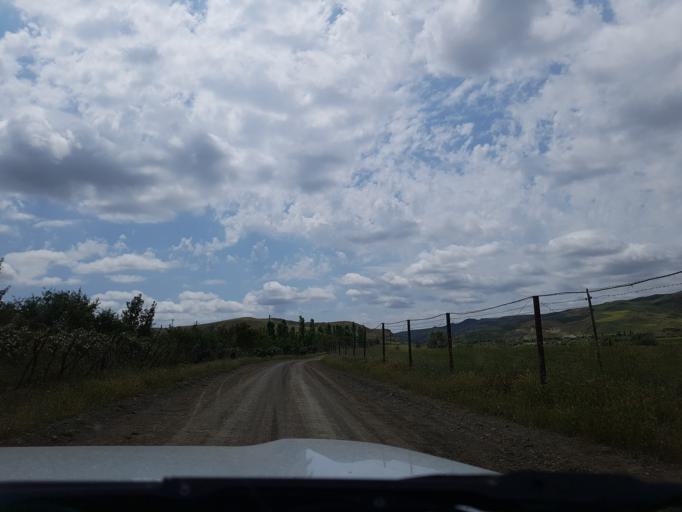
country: TM
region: Ahal
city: Baharly
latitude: 38.2153
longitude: 56.9943
